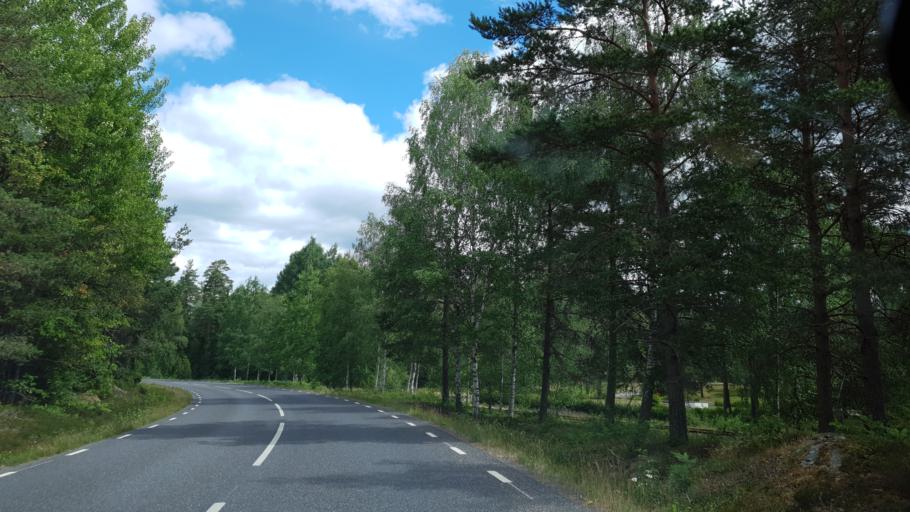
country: SE
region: Kronoberg
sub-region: Uppvidinge Kommun
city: Aseda
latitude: 57.1722
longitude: 15.3694
